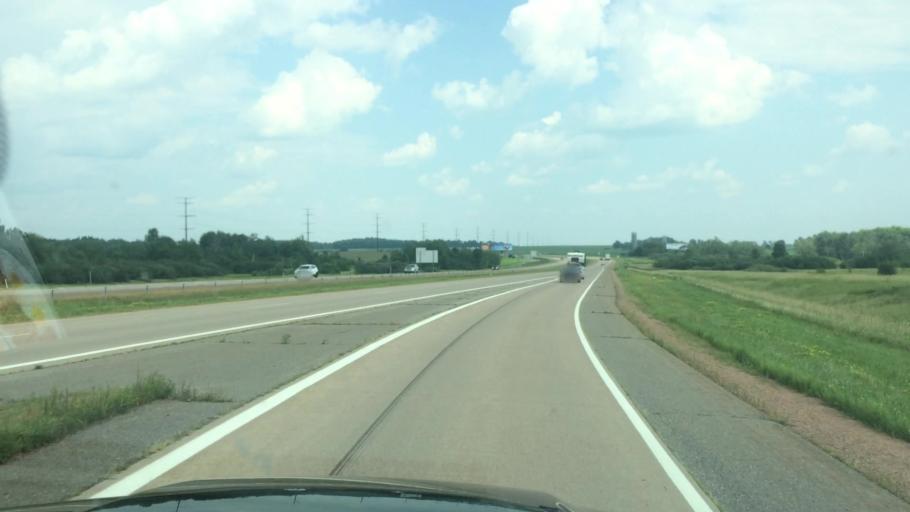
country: US
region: Wisconsin
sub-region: Clark County
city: Abbotsford
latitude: 44.9326
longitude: -90.3088
